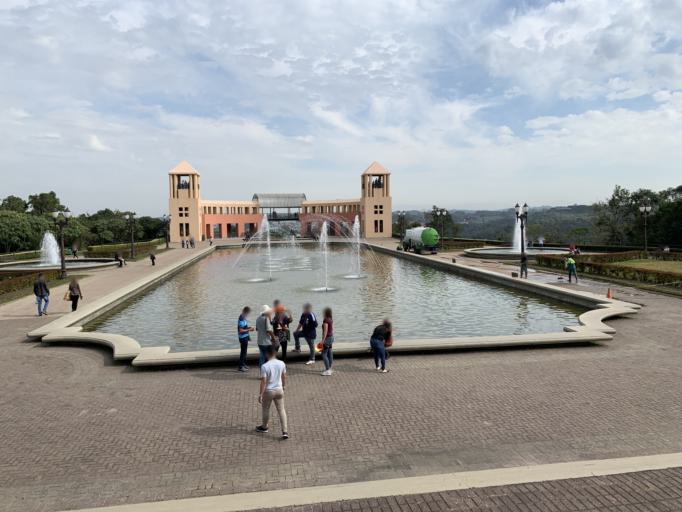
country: BR
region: Parana
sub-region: Curitiba
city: Curitiba
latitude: -25.3791
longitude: -49.2823
